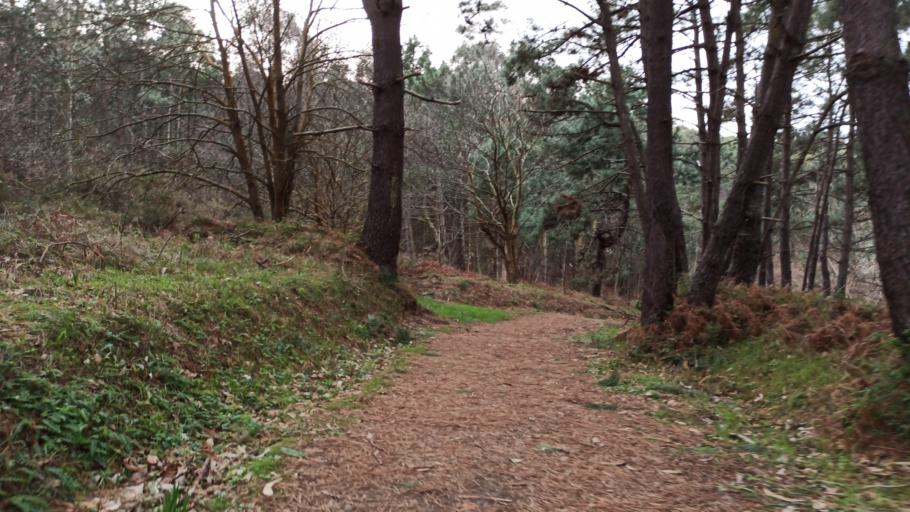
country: ES
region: Galicia
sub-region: Provincia da Coruna
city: Oleiros
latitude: 43.3964
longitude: -8.3340
